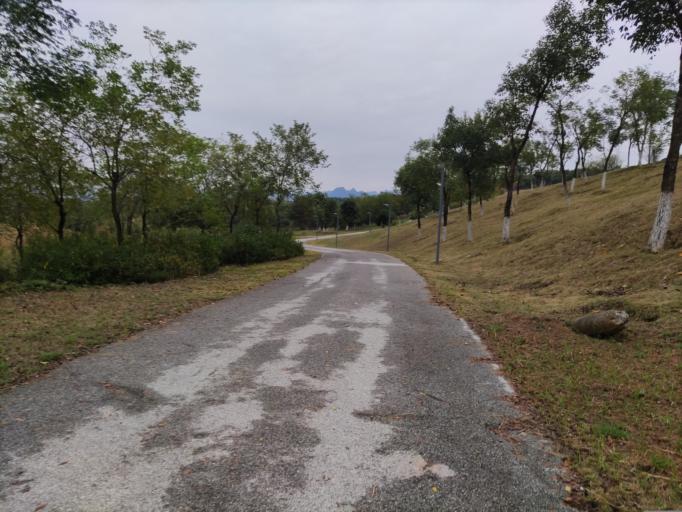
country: CN
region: Guangxi Zhuangzu Zizhiqu
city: Tianzhou
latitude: 23.7821
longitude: 106.7316
